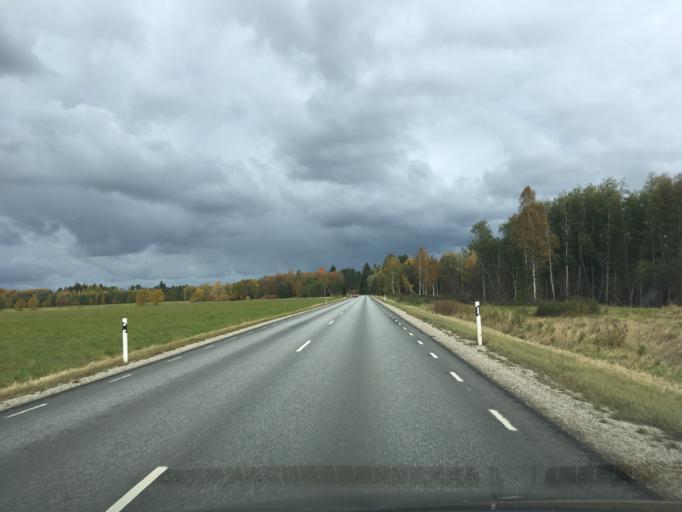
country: EE
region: Harju
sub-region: Anija vald
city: Kehra
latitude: 59.2875
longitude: 25.3751
